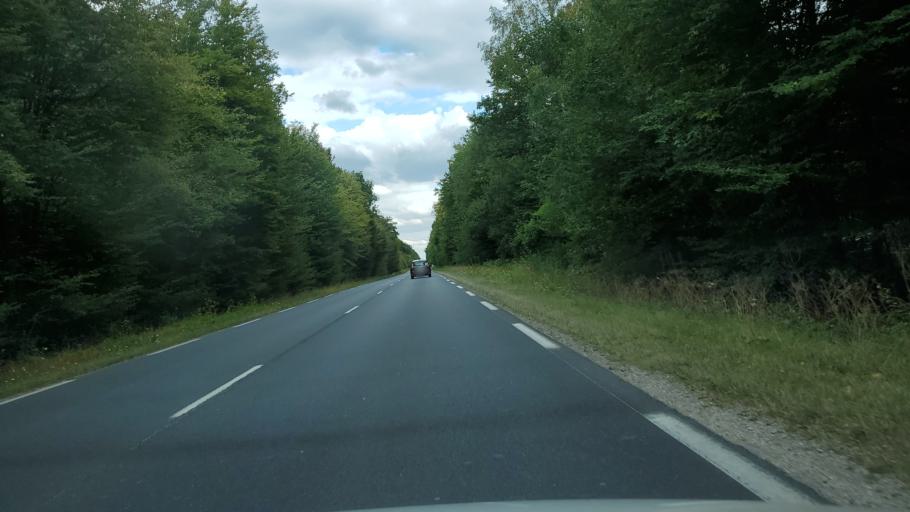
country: FR
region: Ile-de-France
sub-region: Departement de Seine-et-Marne
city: Villeneuve-le-Comte
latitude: 48.7988
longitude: 2.8554
